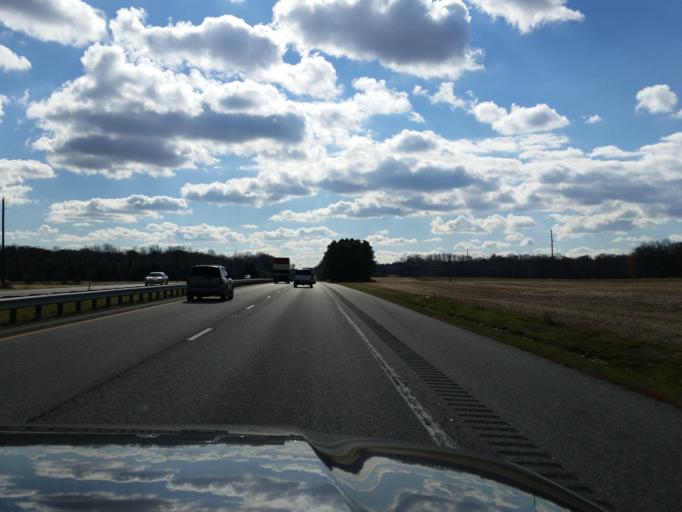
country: US
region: Maryland
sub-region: Queen Anne's County
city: Centreville
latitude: 38.9234
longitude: -76.0624
